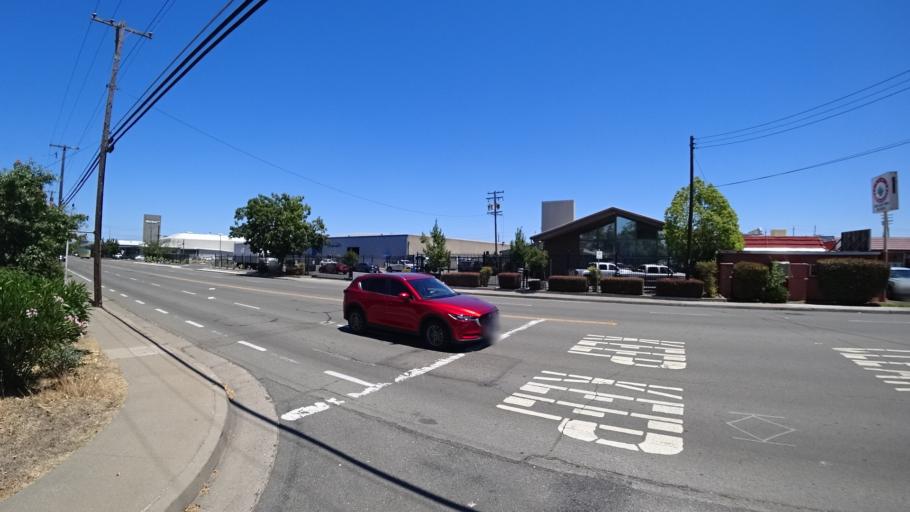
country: US
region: California
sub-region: Sacramento County
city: Parkway
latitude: 38.5292
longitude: -121.4834
